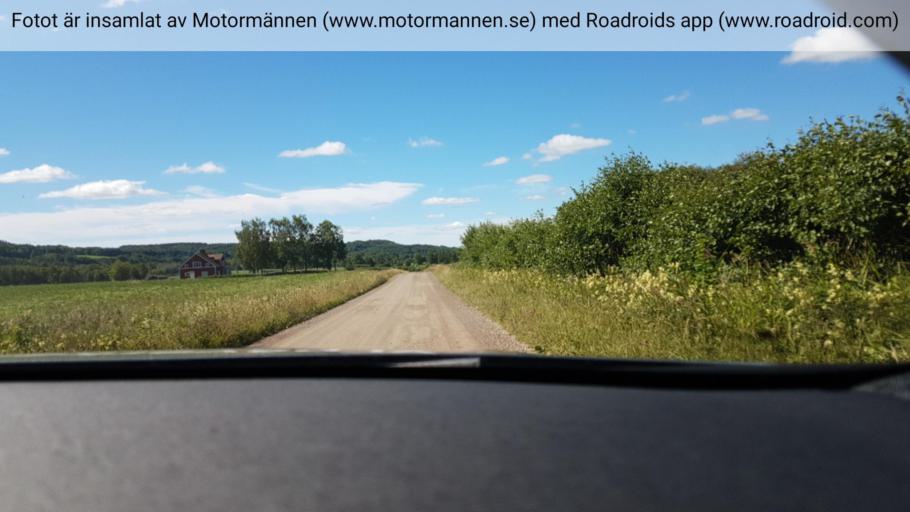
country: SE
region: Vaestra Goetaland
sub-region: Falkopings Kommun
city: Akarp
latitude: 58.2085
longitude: 13.7484
